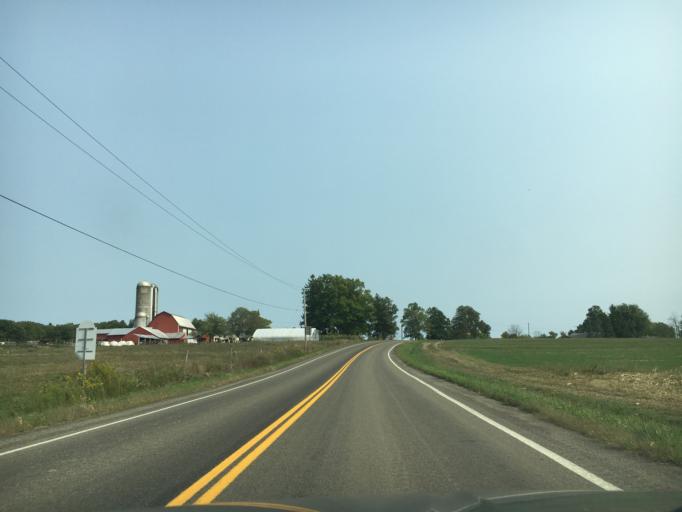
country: US
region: New York
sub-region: Steuben County
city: Sylvan Beach
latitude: 42.4737
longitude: -77.1124
